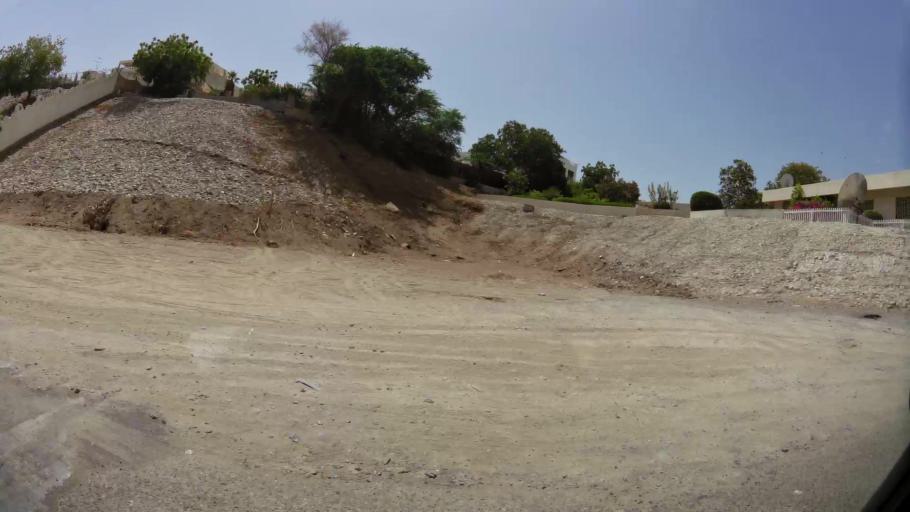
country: OM
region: Muhafazat Masqat
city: Bawshar
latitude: 23.5920
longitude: 58.4522
